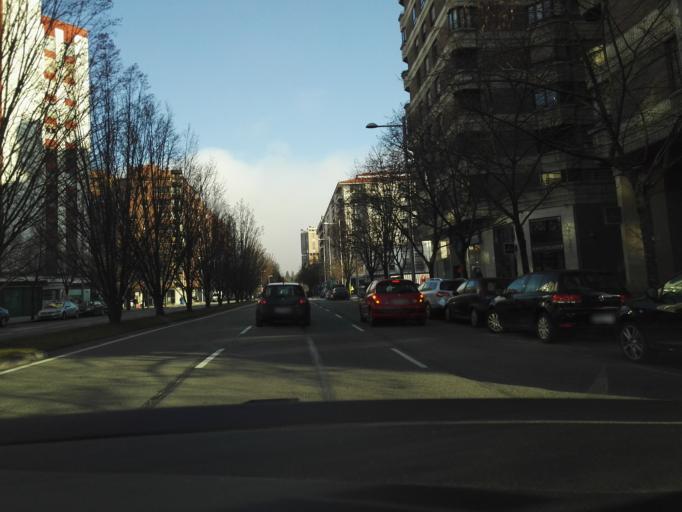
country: ES
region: Navarre
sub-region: Provincia de Navarra
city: Iturrama
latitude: 42.8107
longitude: -1.6567
